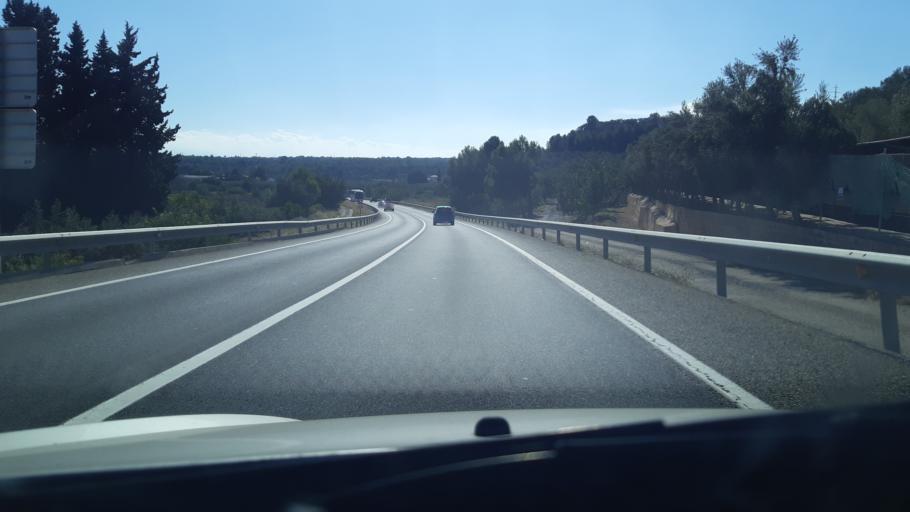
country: ES
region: Catalonia
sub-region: Provincia de Tarragona
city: Tivenys
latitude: 40.9095
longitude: 0.4833
